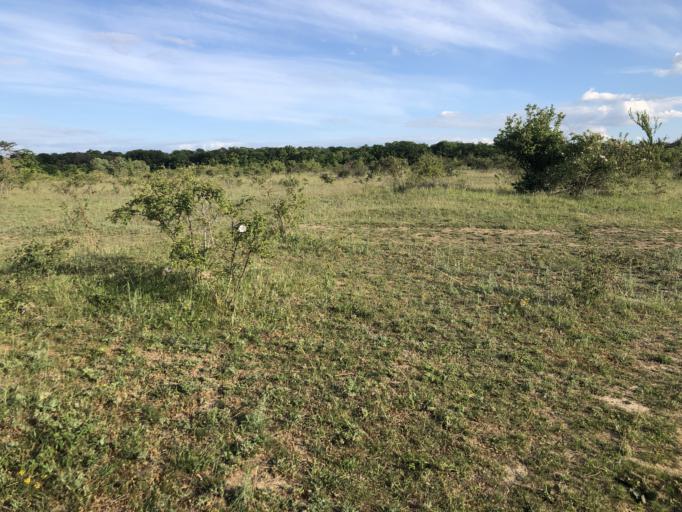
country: DE
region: Saxony-Anhalt
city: Freyburg
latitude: 51.1974
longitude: 11.7494
